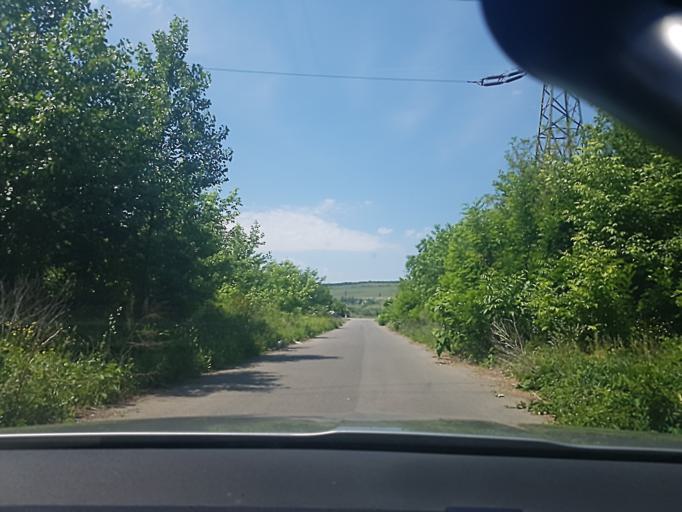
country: RO
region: Hunedoara
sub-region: Comuna Calan
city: Calan
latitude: 45.7390
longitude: 23.0006
